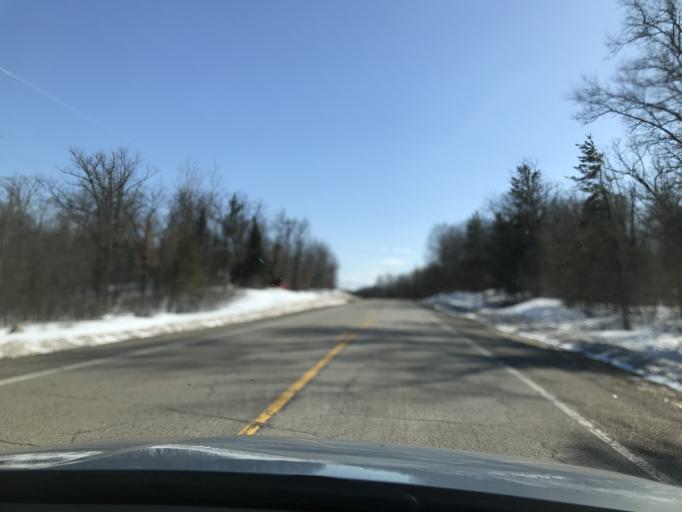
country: US
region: Wisconsin
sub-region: Marinette County
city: Niagara
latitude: 45.3429
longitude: -88.1016
